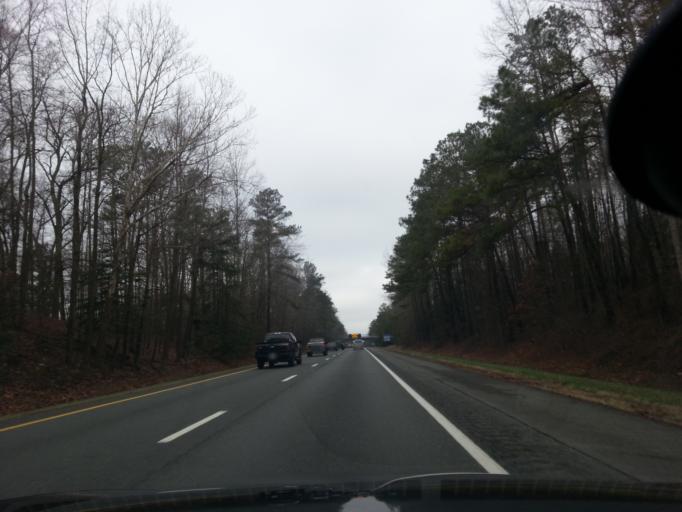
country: US
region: Virginia
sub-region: Henrico County
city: Sandston
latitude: 37.5120
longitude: -77.1564
